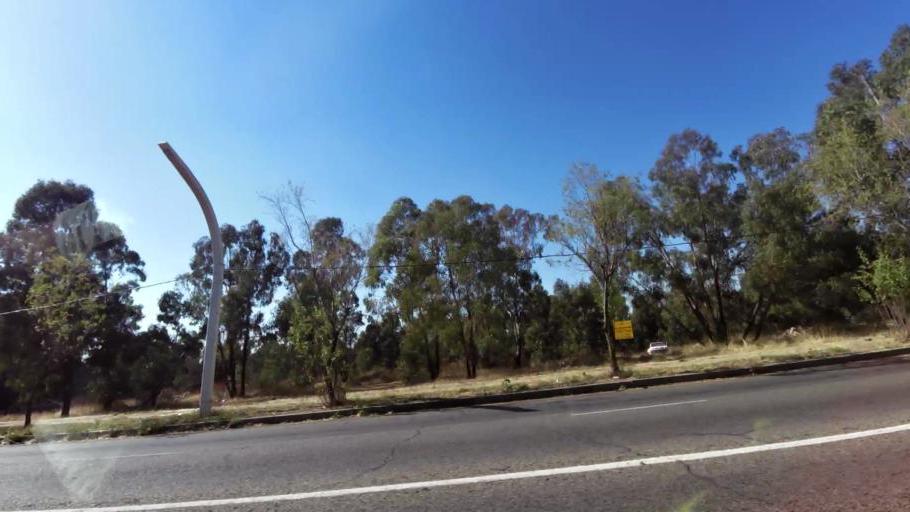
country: ZA
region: Gauteng
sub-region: City of Johannesburg Metropolitan Municipality
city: Johannesburg
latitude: -26.2446
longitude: 27.9854
